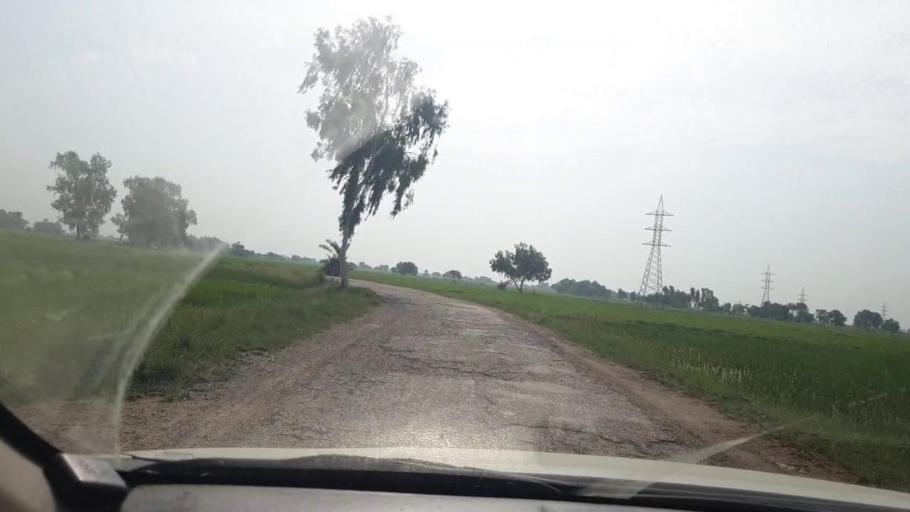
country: PK
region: Sindh
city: Lakhi
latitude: 27.8279
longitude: 68.7363
